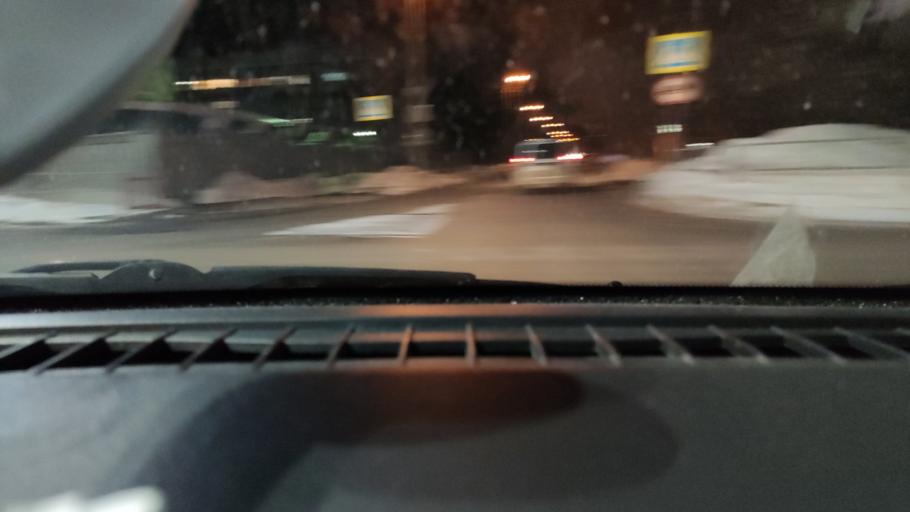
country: RU
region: Perm
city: Krasnokamsk
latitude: 58.0780
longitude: 55.7429
